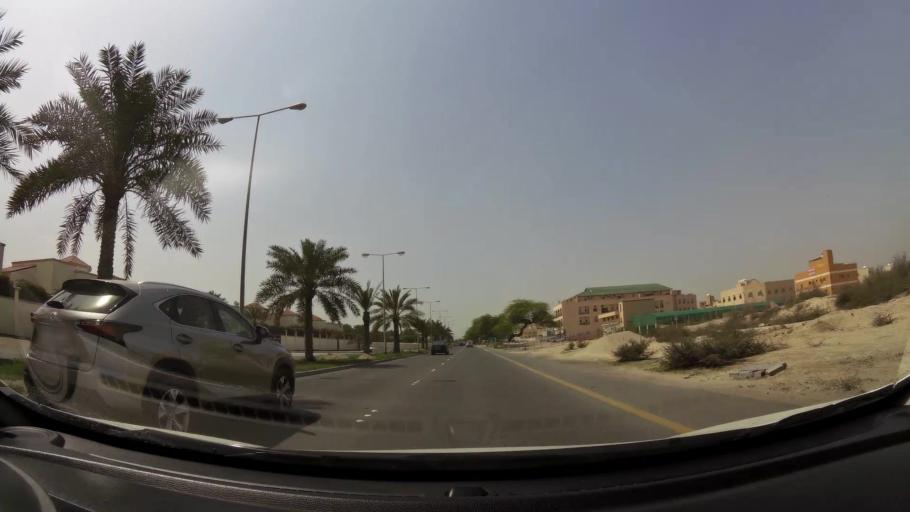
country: BH
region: Manama
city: Jidd Hafs
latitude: 26.2167
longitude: 50.4753
